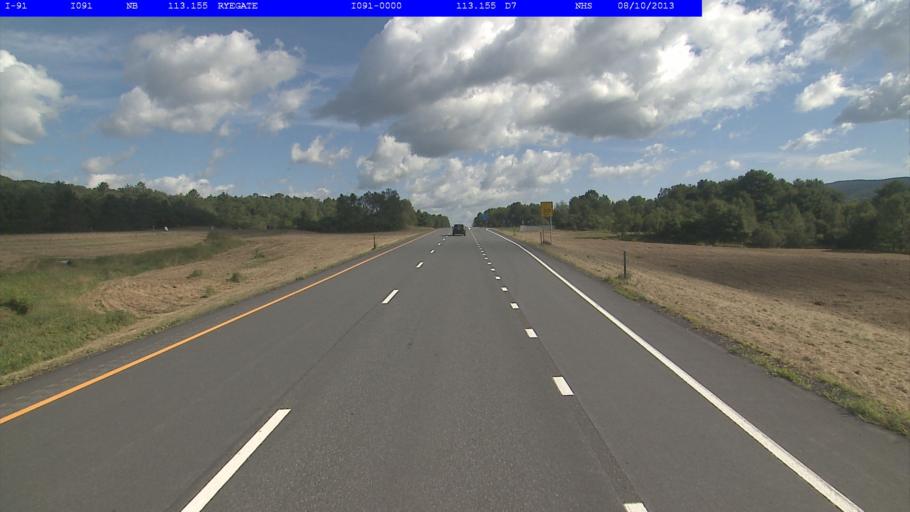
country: US
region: New Hampshire
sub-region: Grafton County
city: Woodsville
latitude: 44.1983
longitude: -72.0709
